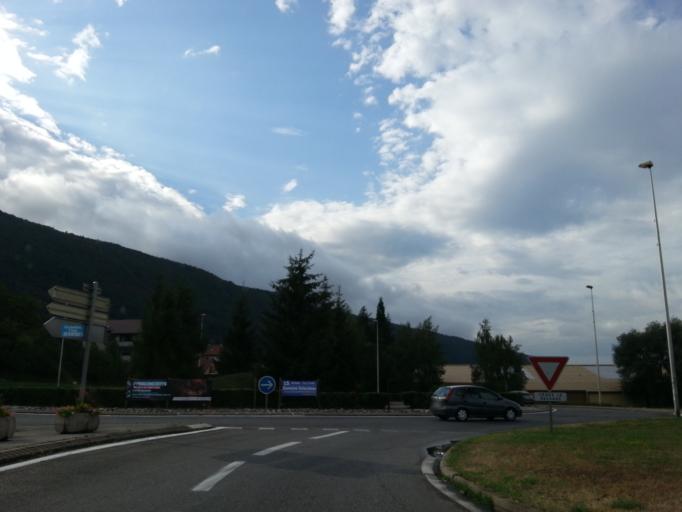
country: FR
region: Rhone-Alpes
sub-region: Departement de la Haute-Savoie
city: Saint-Jorioz
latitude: 45.8452
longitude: 6.1489
